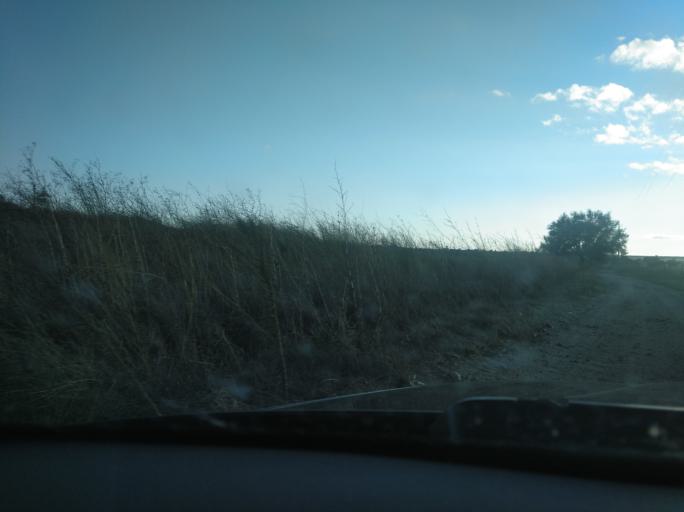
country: PT
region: Portalegre
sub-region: Campo Maior
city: Campo Maior
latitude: 39.0387
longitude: -6.9804
